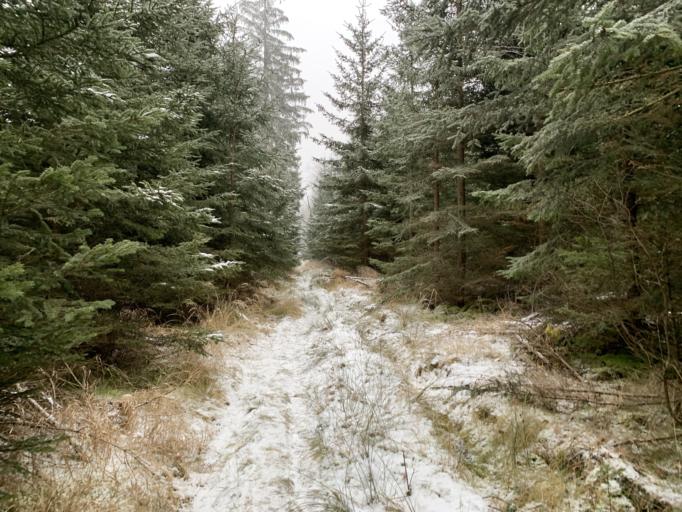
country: CZ
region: Central Bohemia
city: Rozmital pod Tremsinem
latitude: 49.5794
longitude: 13.8141
